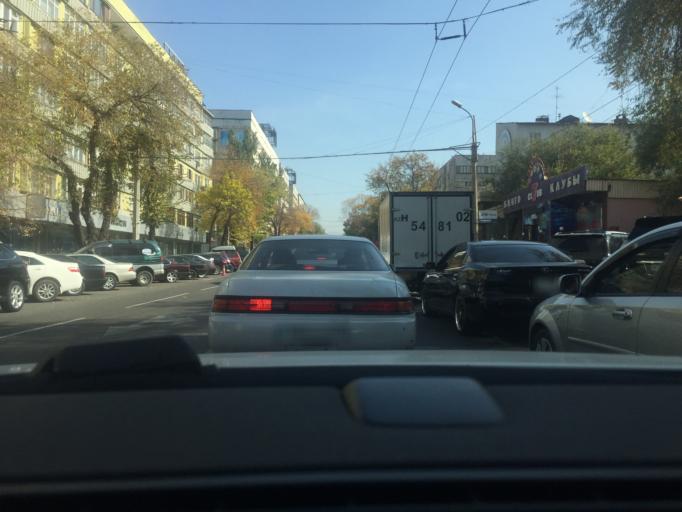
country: KZ
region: Almaty Qalasy
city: Almaty
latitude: 43.2599
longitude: 76.9447
